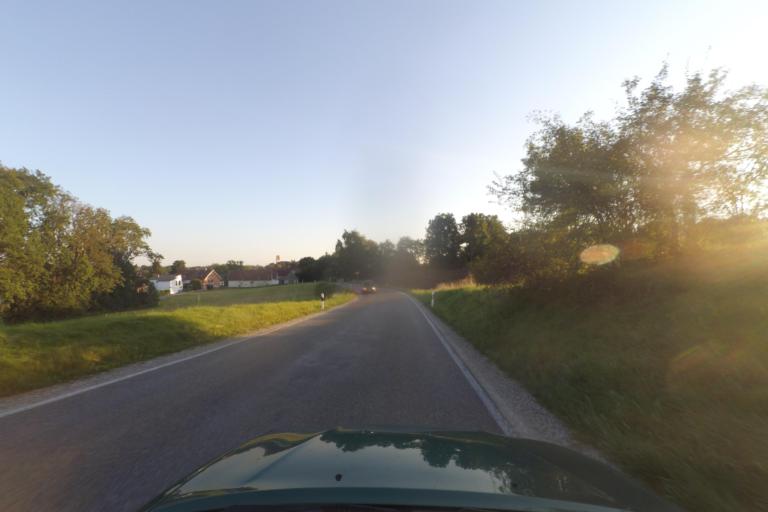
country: DE
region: Bavaria
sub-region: Upper Bavaria
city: Weil
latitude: 48.1035
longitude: 10.9067
